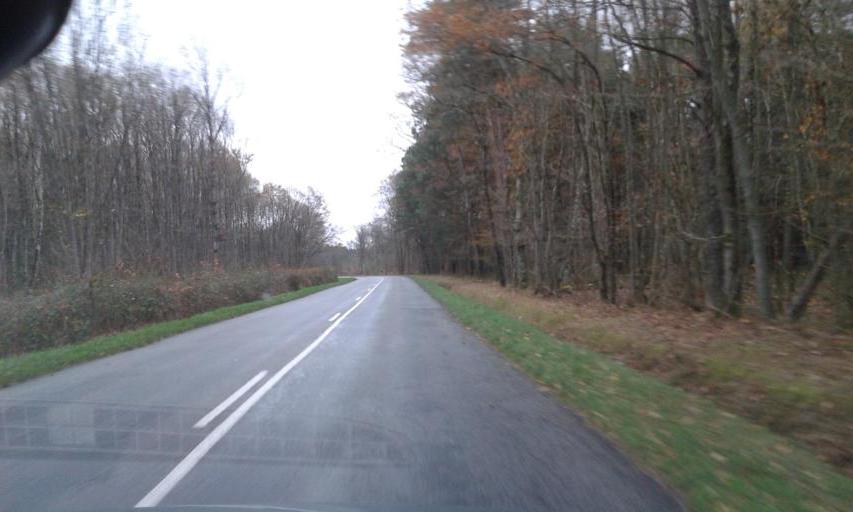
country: FR
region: Centre
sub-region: Departement du Loiret
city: Vitry-aux-Loges
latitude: 47.9027
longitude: 2.2436
